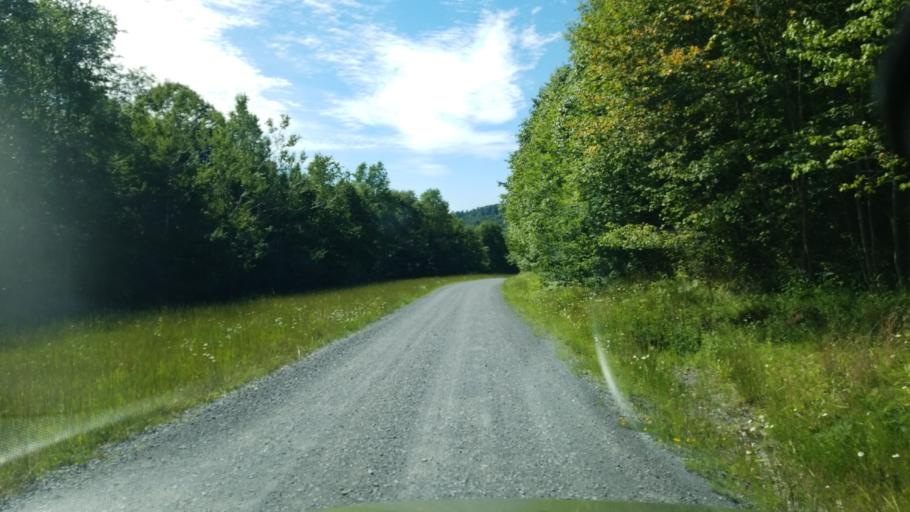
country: US
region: Pennsylvania
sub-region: Clearfield County
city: Clearfield
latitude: 41.2097
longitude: -78.4965
